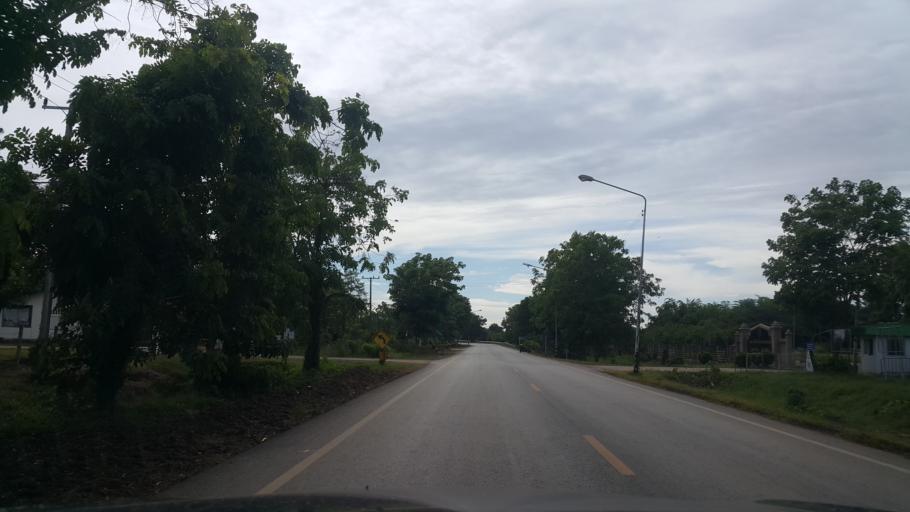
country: TH
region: Sukhothai
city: Si Nakhon
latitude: 17.2772
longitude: 99.9706
